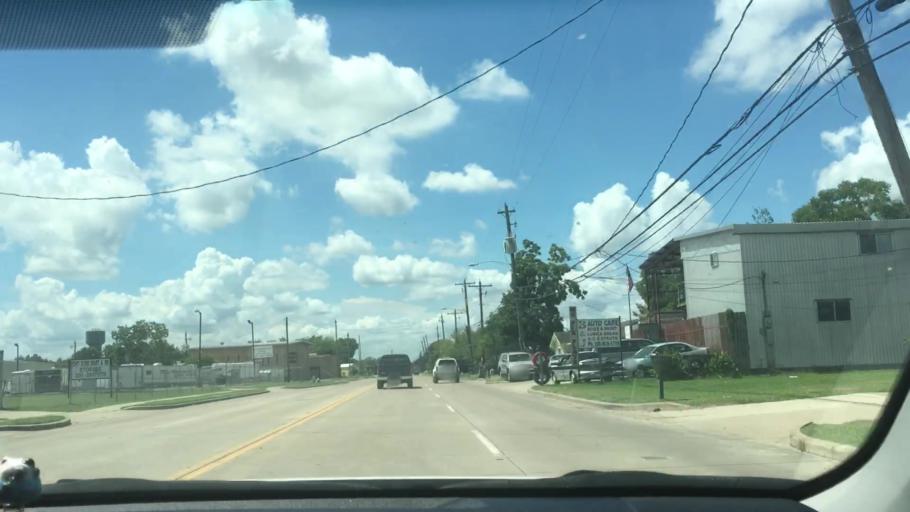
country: US
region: Texas
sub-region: Fort Bend County
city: Fifth Street
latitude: 29.5969
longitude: -95.5572
